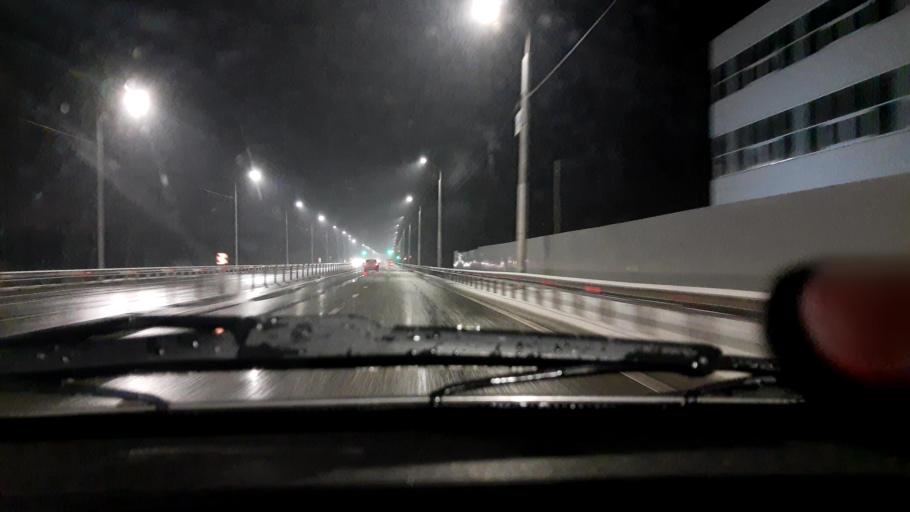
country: RU
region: Bashkortostan
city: Ufa
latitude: 54.6980
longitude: 55.8943
